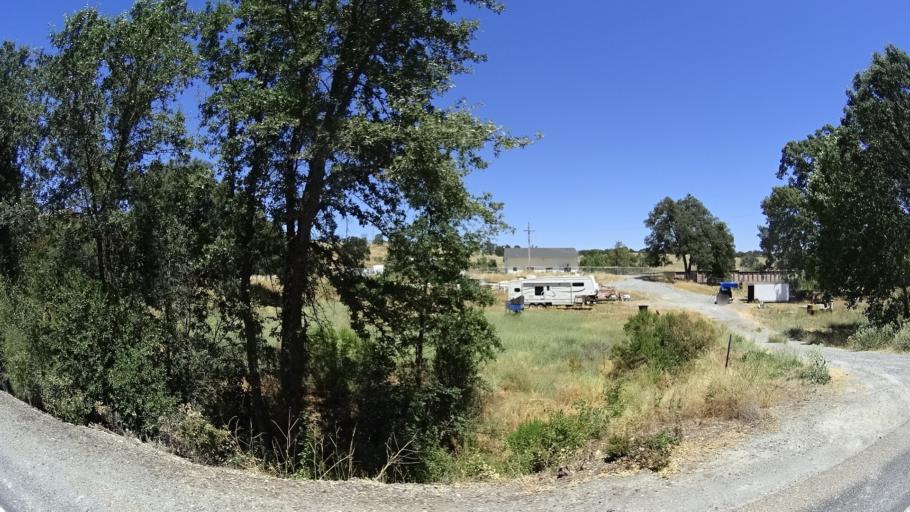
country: US
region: California
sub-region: Calaveras County
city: San Andreas
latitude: 38.1828
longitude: -120.6830
